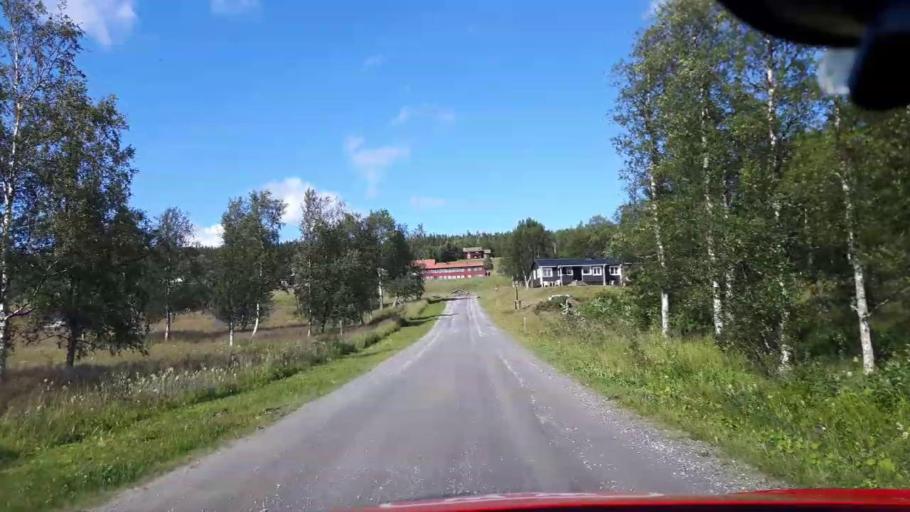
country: SE
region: Jaemtland
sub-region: Are Kommun
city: Are
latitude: 63.2129
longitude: 13.0540
